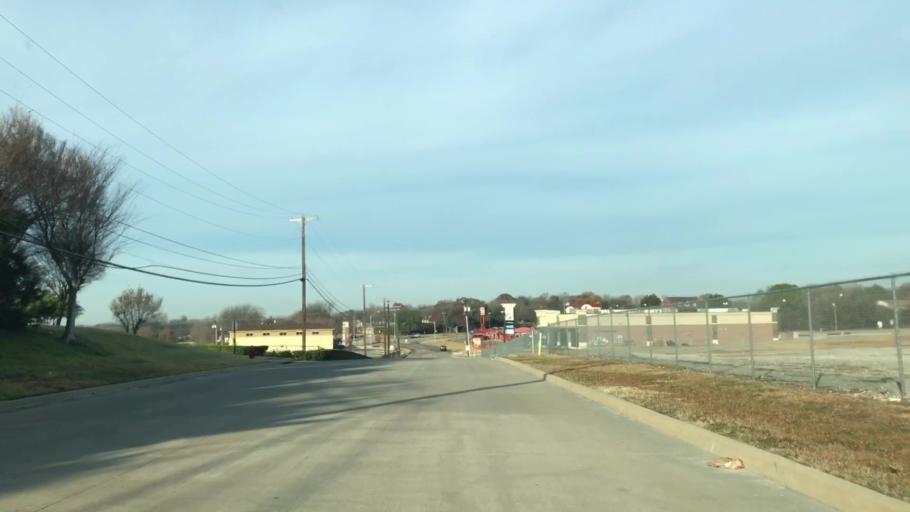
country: US
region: Texas
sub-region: Tarrant County
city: Sansom Park
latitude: 32.8169
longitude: -97.4168
